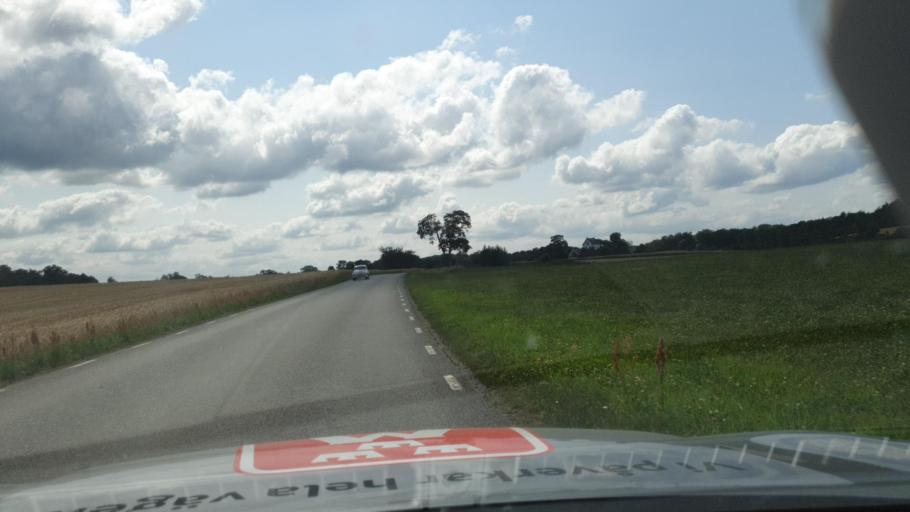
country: SE
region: Skane
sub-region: Hassleholms Kommun
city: Vinslov
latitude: 56.0686
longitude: 13.8421
